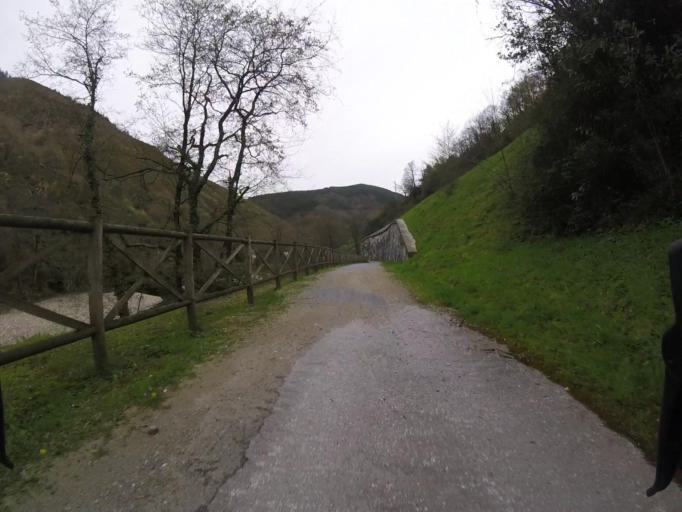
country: ES
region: Navarre
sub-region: Provincia de Navarra
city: Bera
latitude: 43.2964
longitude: -1.7308
